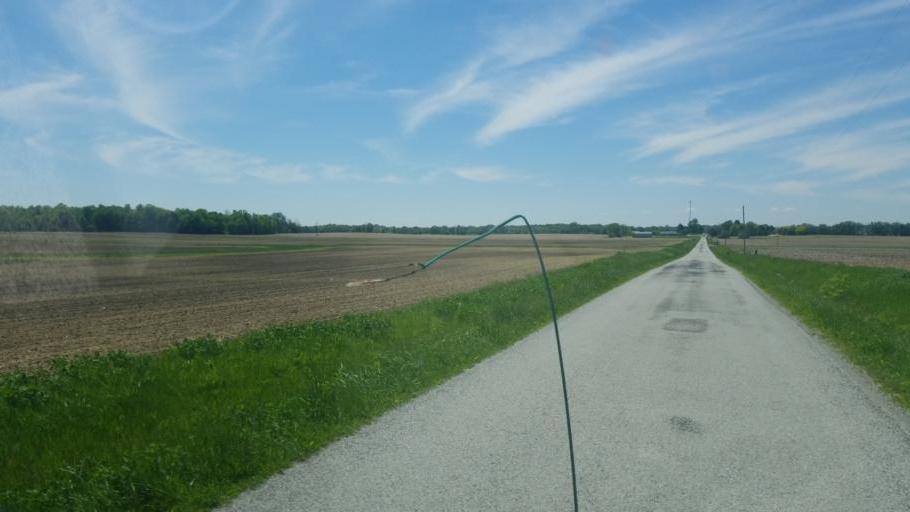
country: US
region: Ohio
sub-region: Huron County
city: Greenwich
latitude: 41.1191
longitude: -82.5906
